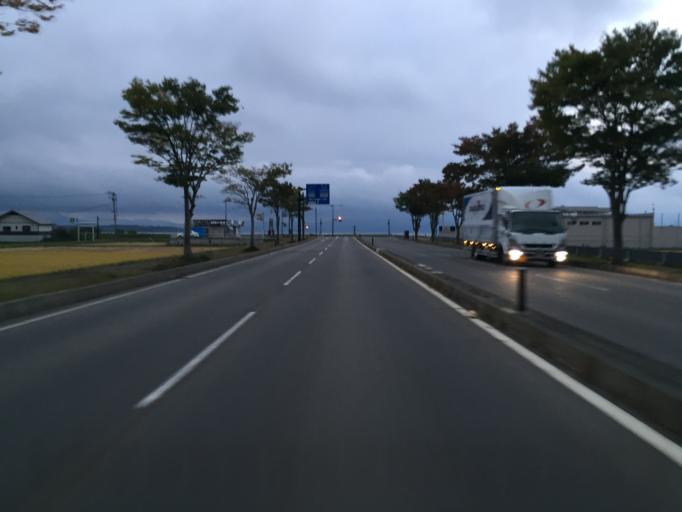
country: JP
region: Fukushima
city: Inawashiro
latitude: 37.5363
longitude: 140.1082
